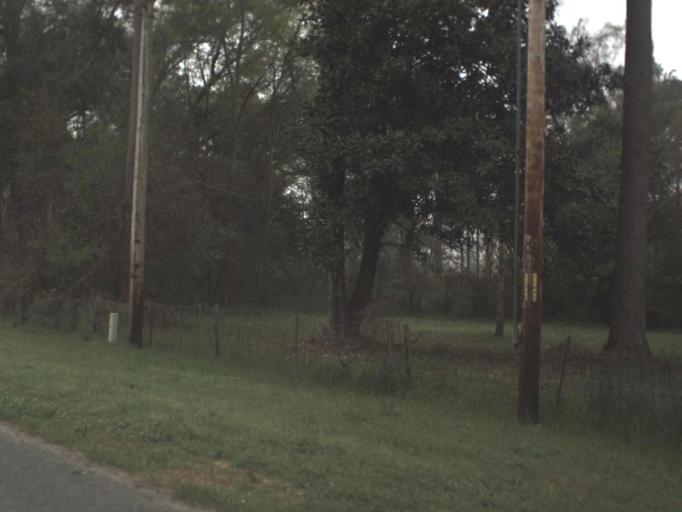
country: US
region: Florida
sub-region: Gadsden County
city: Gretna
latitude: 30.5347
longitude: -84.6847
